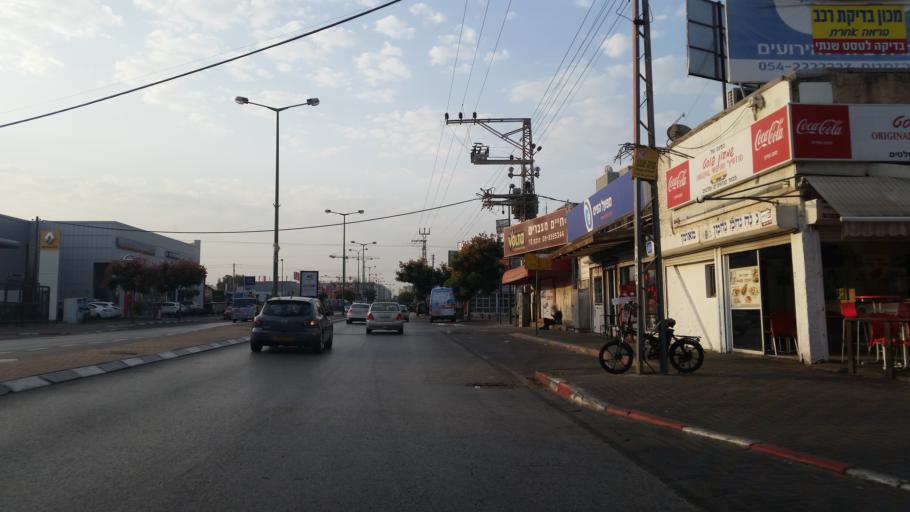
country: IL
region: Central District
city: Bet Yizhaq
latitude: 32.3198
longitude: 34.8742
